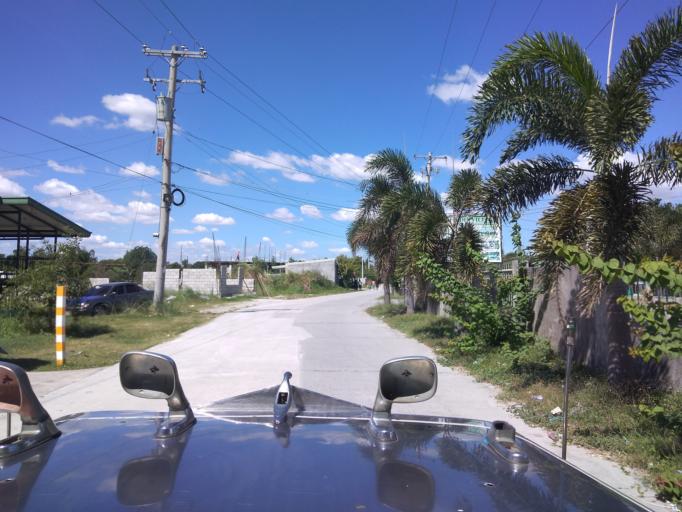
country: PH
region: Central Luzon
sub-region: Province of Pampanga
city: Magliman
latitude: 15.0281
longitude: 120.6509
